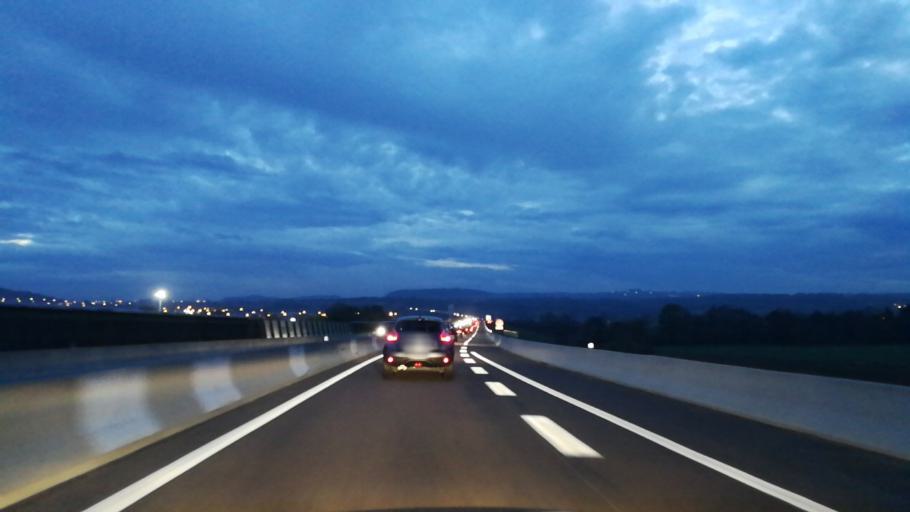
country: FR
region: Bourgogne
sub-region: Departement de la Cote-d'Or
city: Ahuy
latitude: 47.3588
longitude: 5.0401
